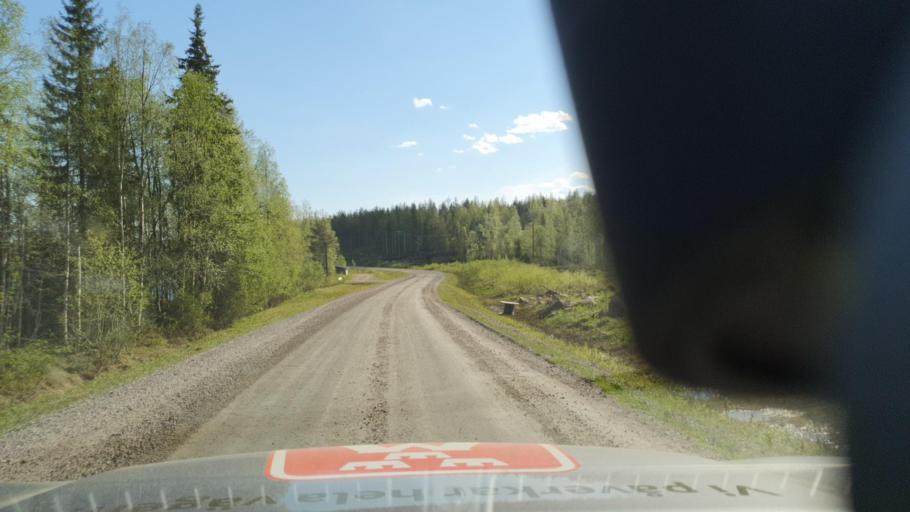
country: SE
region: Norrbotten
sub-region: Bodens Kommun
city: Boden
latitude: 66.4716
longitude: 21.8718
